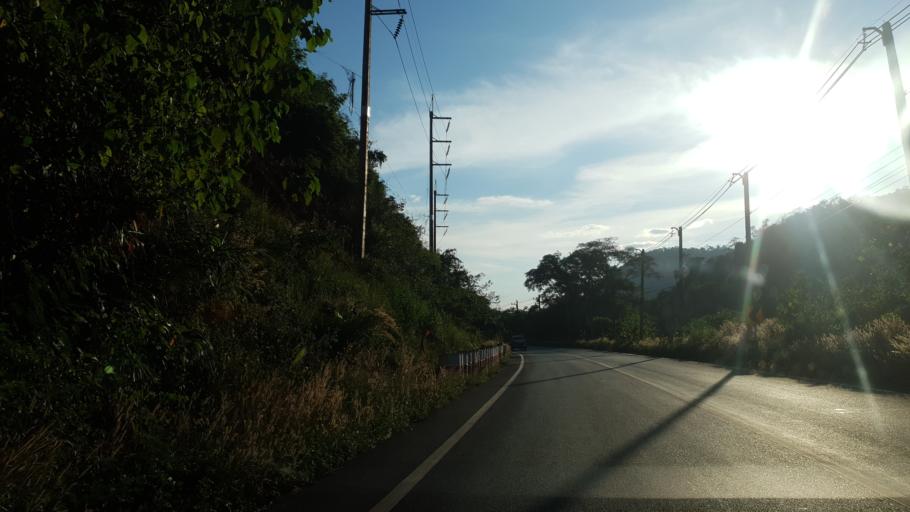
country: TH
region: Loei
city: Dan Sai
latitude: 17.2211
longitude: 101.0254
